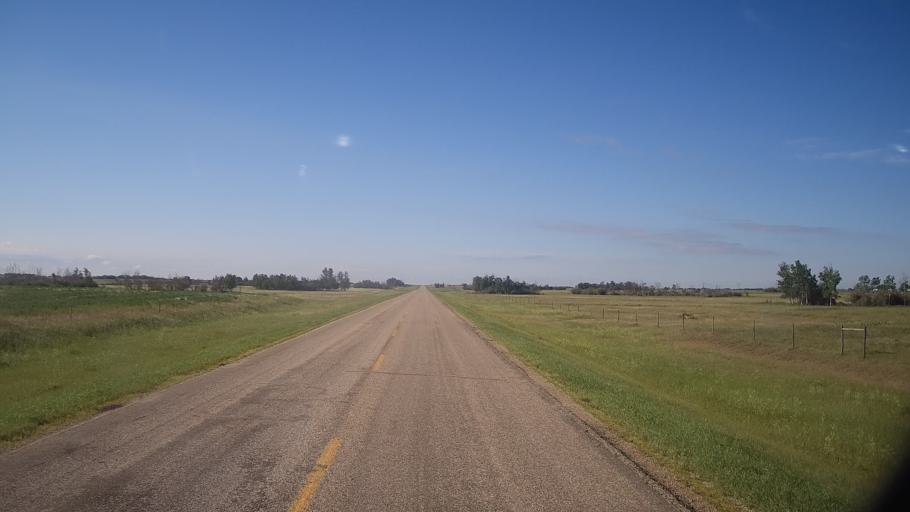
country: CA
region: Saskatchewan
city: Watrous
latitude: 51.7602
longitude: -105.2867
